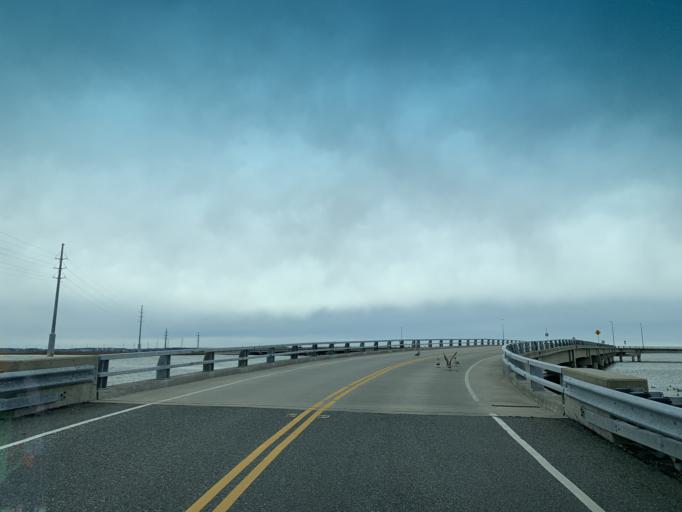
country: US
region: Virginia
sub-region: Accomack County
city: Chincoteague
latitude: 37.9358
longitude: -75.3802
